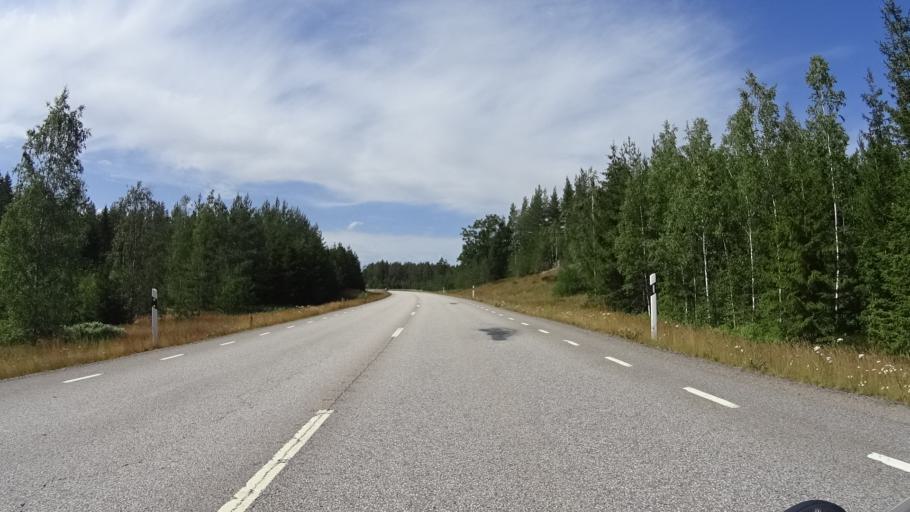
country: SE
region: Kalmar
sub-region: Vasterviks Kommun
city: Gamleby
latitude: 57.9552
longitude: 16.3754
